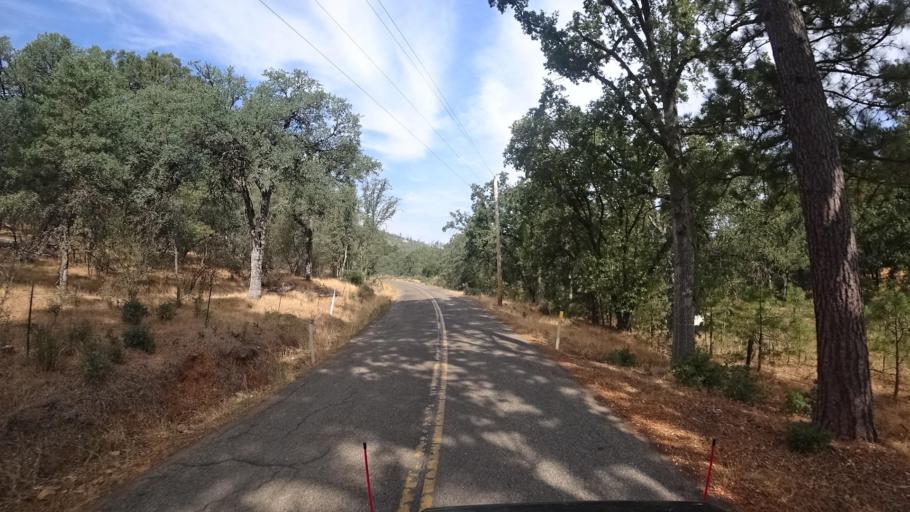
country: US
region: California
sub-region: Mariposa County
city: Mariposa
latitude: 37.5399
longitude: -119.9889
